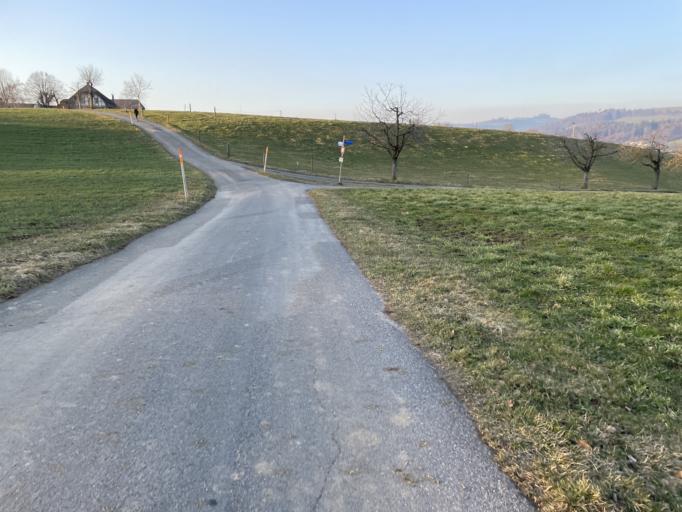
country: CH
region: Bern
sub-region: Bern-Mittelland District
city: Worb
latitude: 46.9215
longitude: 7.5584
